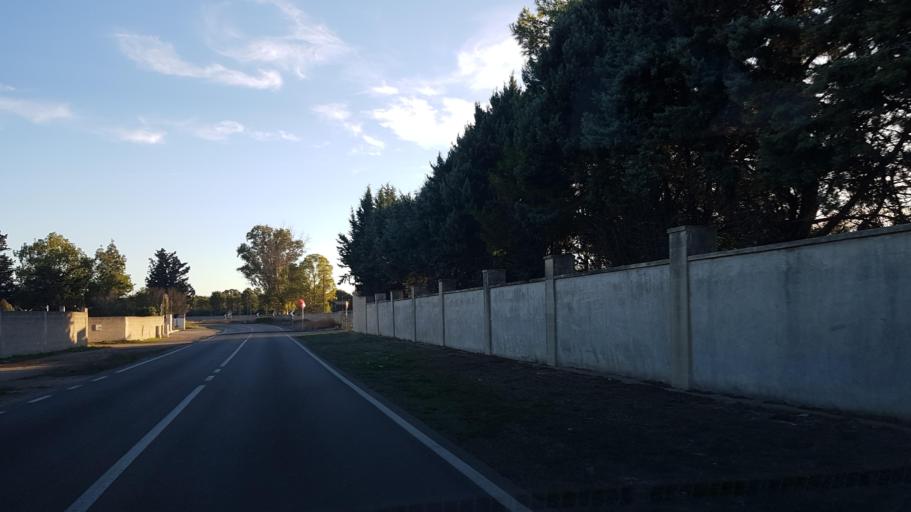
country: IT
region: Apulia
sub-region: Provincia di Lecce
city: Giorgilorio
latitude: 40.3978
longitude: 18.1951
